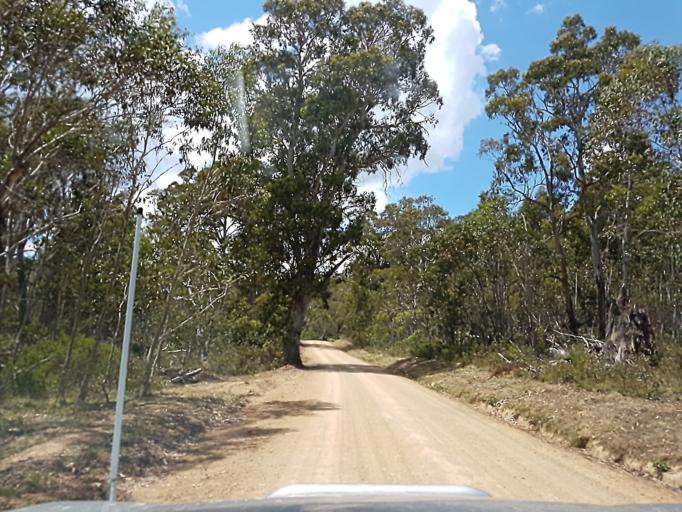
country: AU
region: New South Wales
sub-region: Snowy River
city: Jindabyne
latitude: -36.8781
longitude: 148.0751
